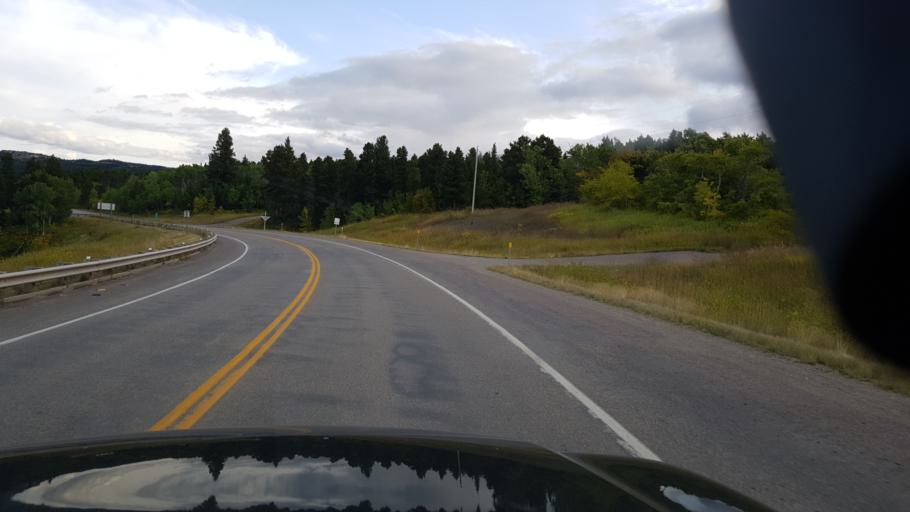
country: US
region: Montana
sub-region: Glacier County
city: South Browning
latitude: 48.4389
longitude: -113.2190
